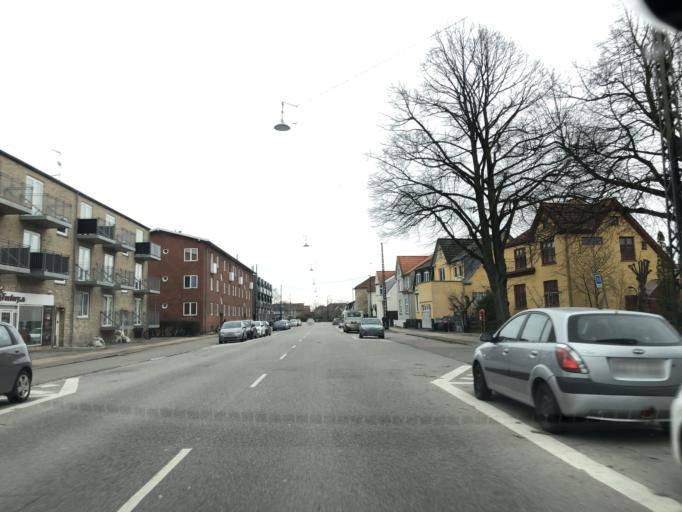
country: DK
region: Capital Region
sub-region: Tarnby Kommune
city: Tarnby
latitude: 55.6501
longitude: 12.6210
